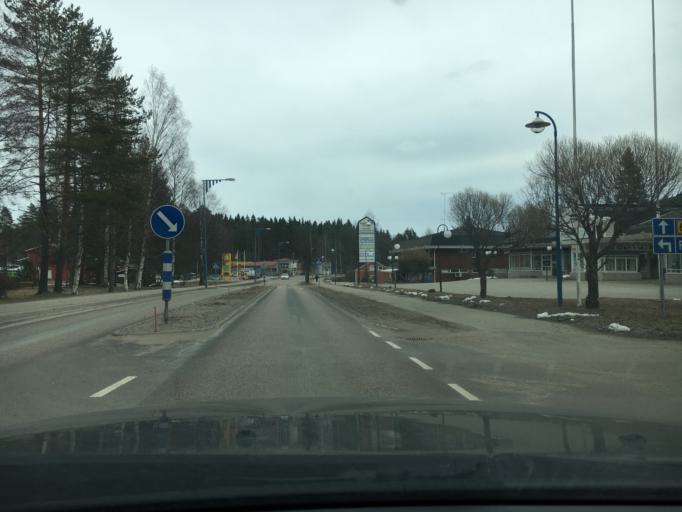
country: FI
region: Central Finland
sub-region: AEaenekoski
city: Konnevesi
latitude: 62.6281
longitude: 26.2878
